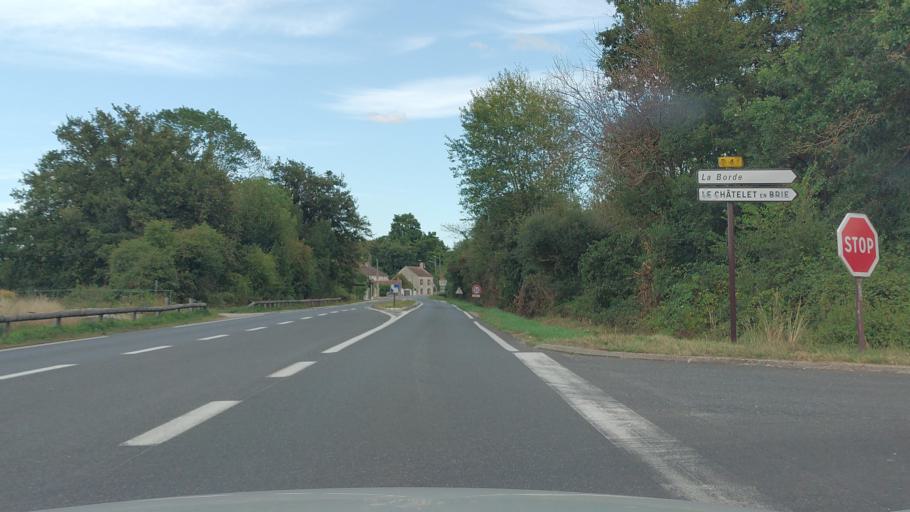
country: FR
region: Ile-de-France
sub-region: Departement de Seine-et-Marne
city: Le Chatelet-en-Brie
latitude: 48.5431
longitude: 2.8040
